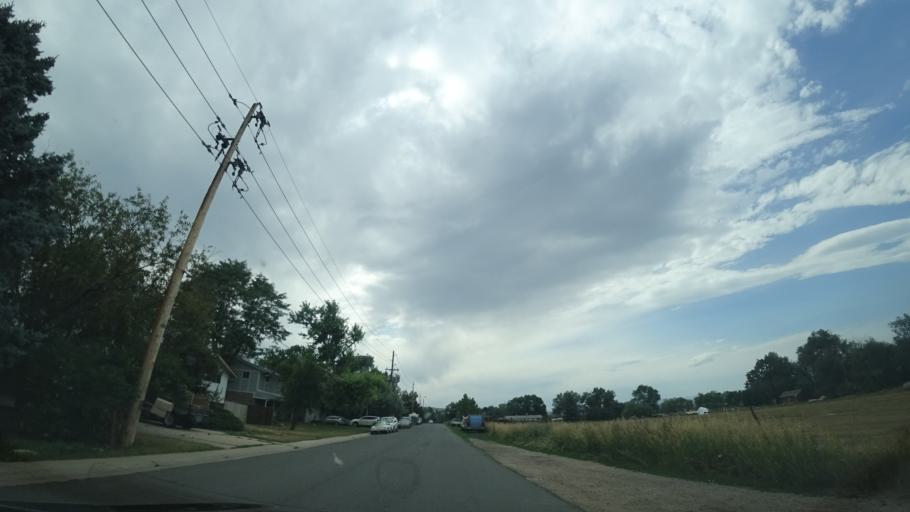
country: US
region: Colorado
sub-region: Jefferson County
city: Lakewood
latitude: 39.7093
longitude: -105.1005
